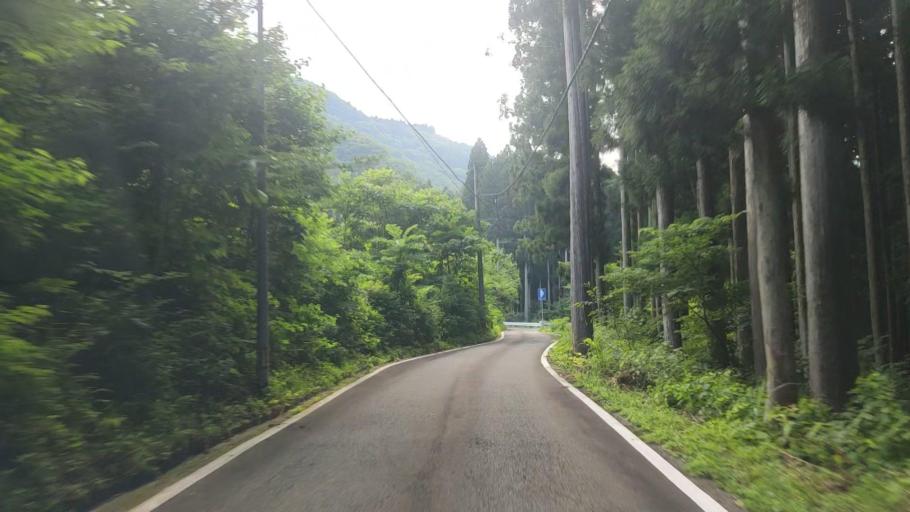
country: JP
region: Fukui
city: Katsuyama
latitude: 36.2248
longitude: 136.5310
